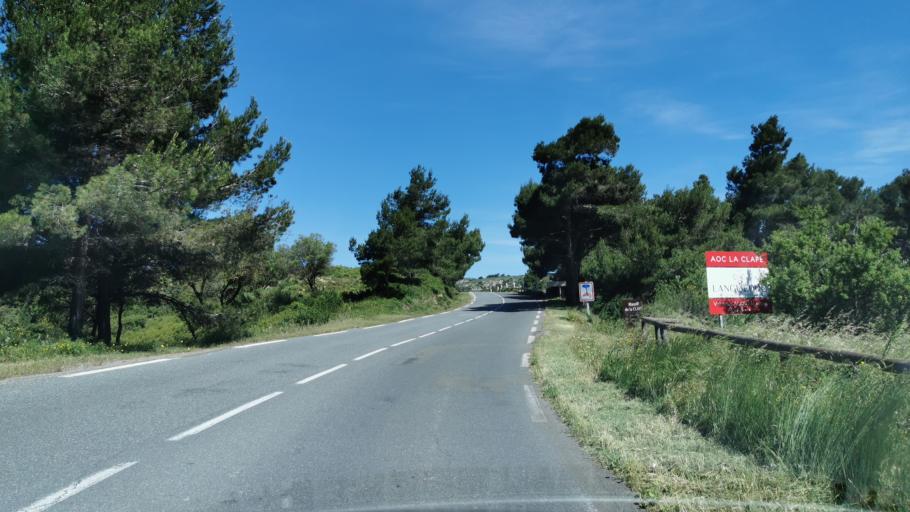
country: FR
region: Languedoc-Roussillon
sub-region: Departement de l'Aude
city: Armissan
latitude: 43.1568
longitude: 3.1522
